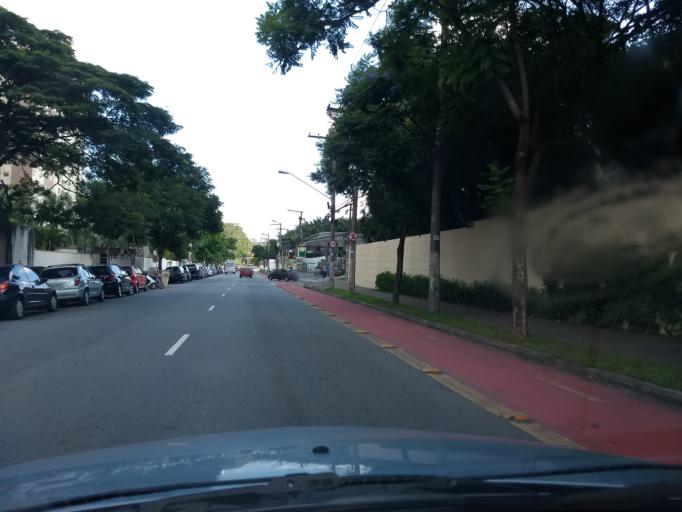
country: BR
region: Sao Paulo
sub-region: Osasco
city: Osasco
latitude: -23.5519
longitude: -46.7436
